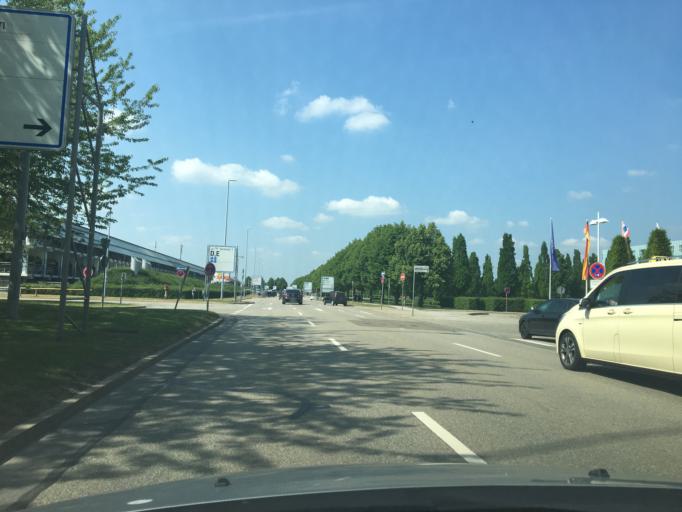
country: DE
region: Bavaria
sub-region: Upper Bavaria
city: Hallbergmoos
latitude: 48.3543
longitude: 11.7870
